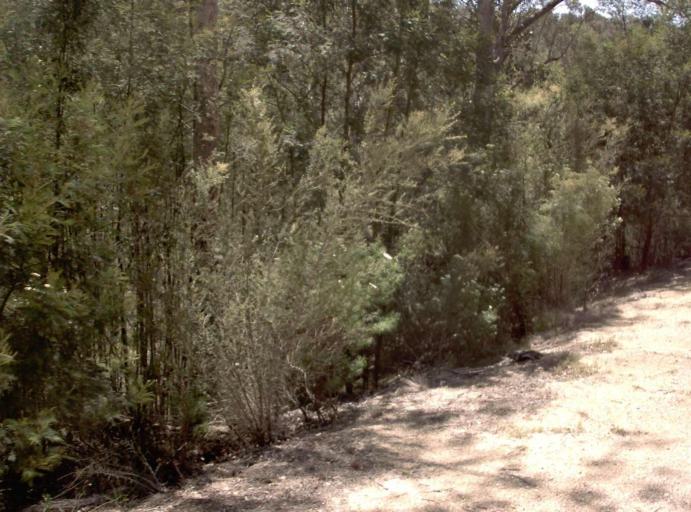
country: AU
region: Victoria
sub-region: East Gippsland
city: Bairnsdale
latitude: -37.4582
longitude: 147.8280
